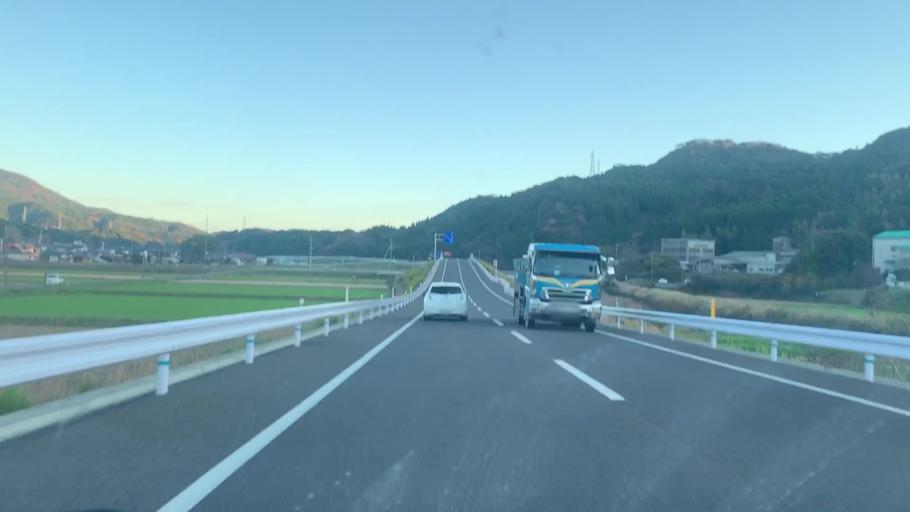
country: JP
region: Saga Prefecture
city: Takeocho-takeo
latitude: 33.2541
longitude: 129.9880
